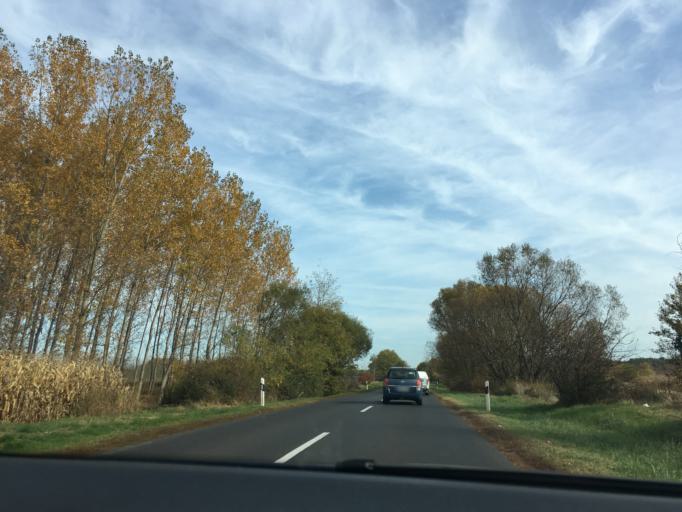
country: HU
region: Szabolcs-Szatmar-Bereg
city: Kallosemjen
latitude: 47.8568
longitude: 21.9661
